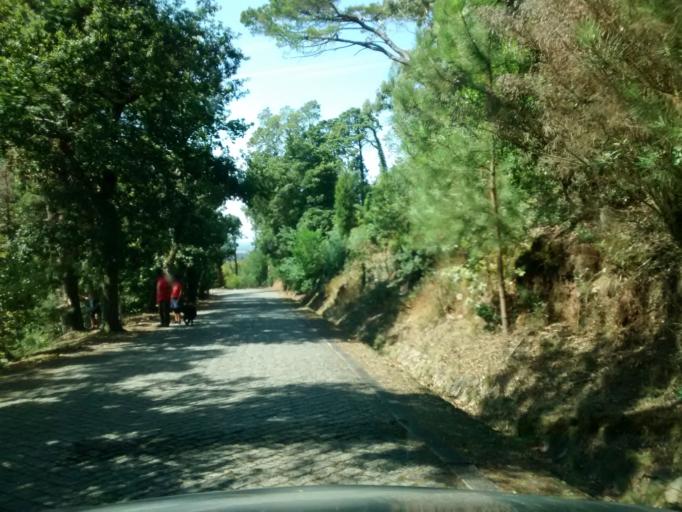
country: PT
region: Aveiro
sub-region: Mealhada
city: Pampilhosa do Botao
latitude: 40.3801
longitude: -8.3756
